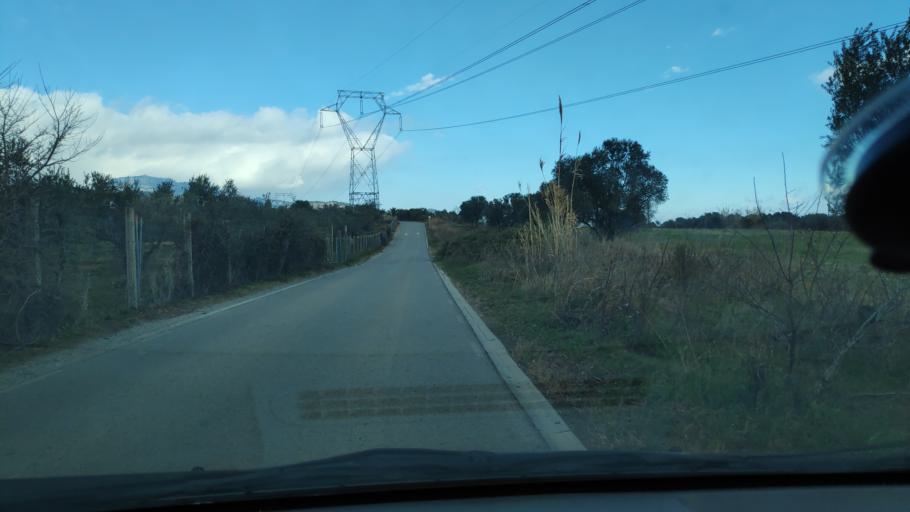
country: ES
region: Catalonia
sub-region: Provincia de Barcelona
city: Terrassa
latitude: 41.5791
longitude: 1.9872
